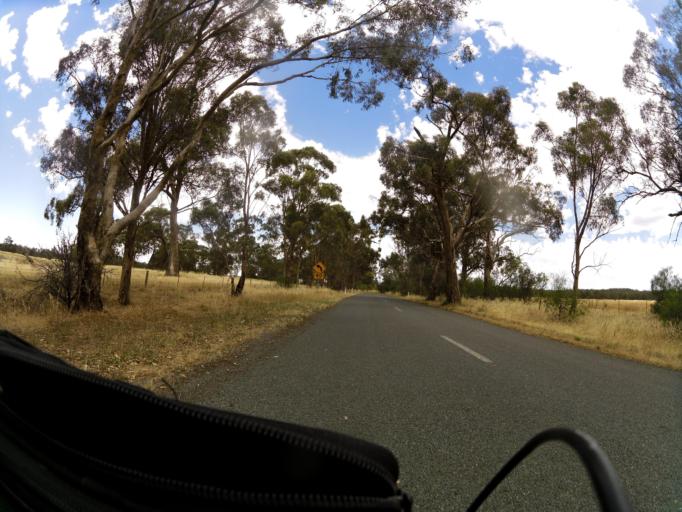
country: AU
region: Victoria
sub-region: Greater Shepparton
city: Shepparton
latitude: -36.6542
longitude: 145.2022
